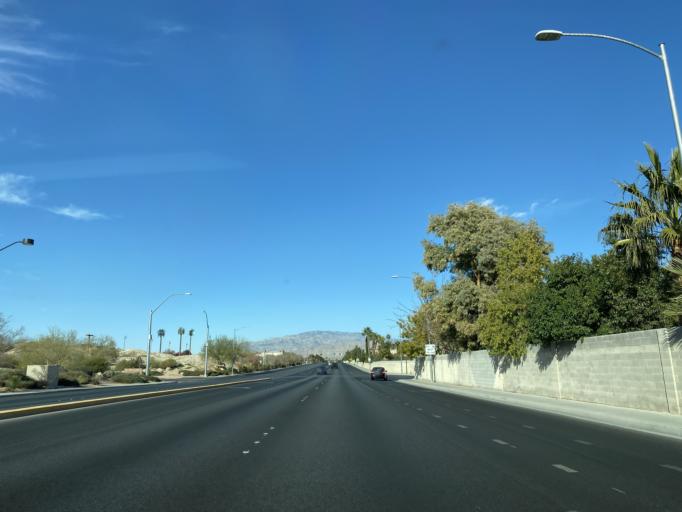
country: US
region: Nevada
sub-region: Clark County
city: Las Vegas
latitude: 36.2833
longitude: -115.2605
